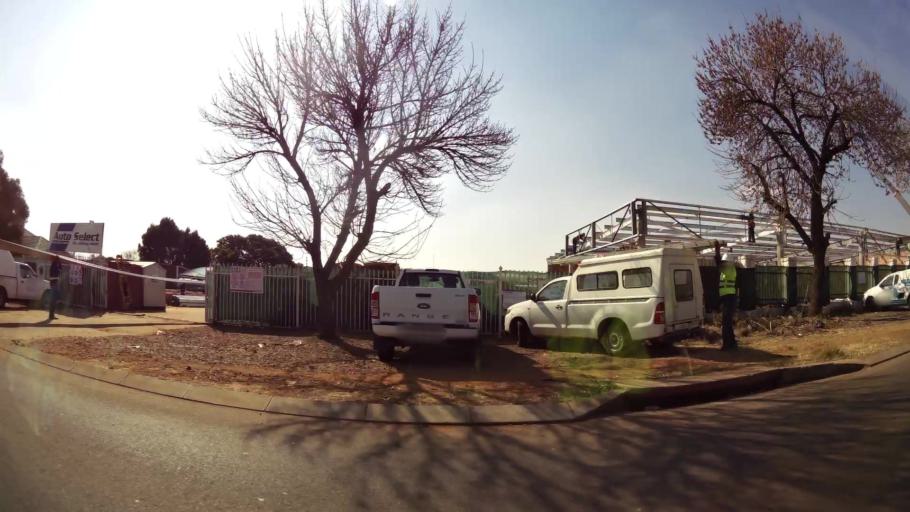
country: ZA
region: Gauteng
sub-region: City of Johannesburg Metropolitan Municipality
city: Modderfontein
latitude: -26.1243
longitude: 28.2275
